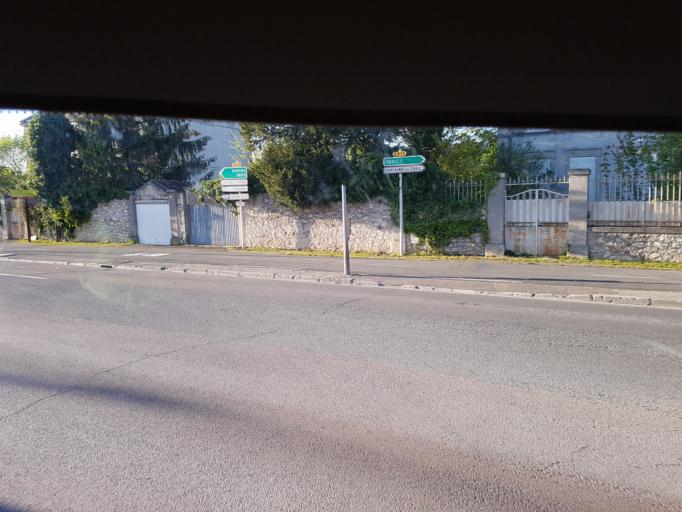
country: FR
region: Champagne-Ardenne
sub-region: Departement de l'Aube
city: Romilly-sur-Seine
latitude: 48.5105
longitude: 3.7258
